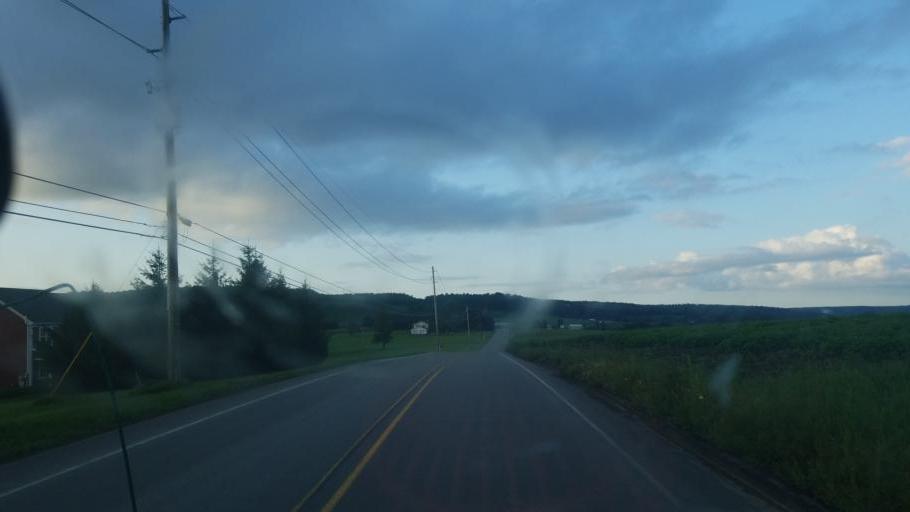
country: US
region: Pennsylvania
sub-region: Potter County
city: Galeton
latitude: 41.8642
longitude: -77.7660
